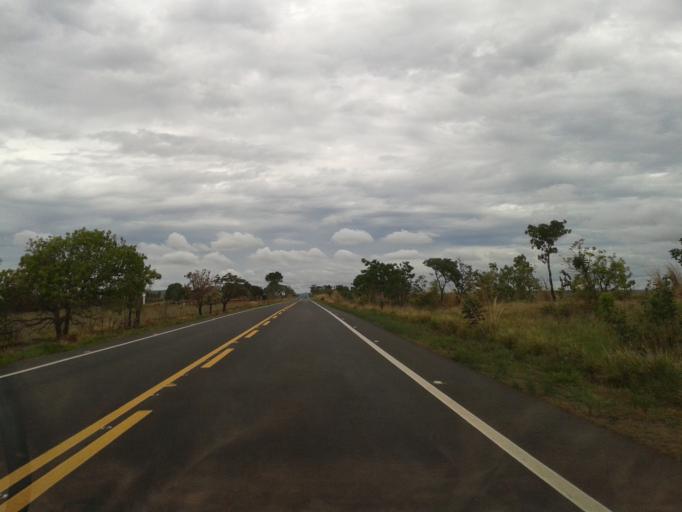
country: BR
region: Goias
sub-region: Caldas Novas
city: Caldas Novas
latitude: -17.8871
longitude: -48.6522
